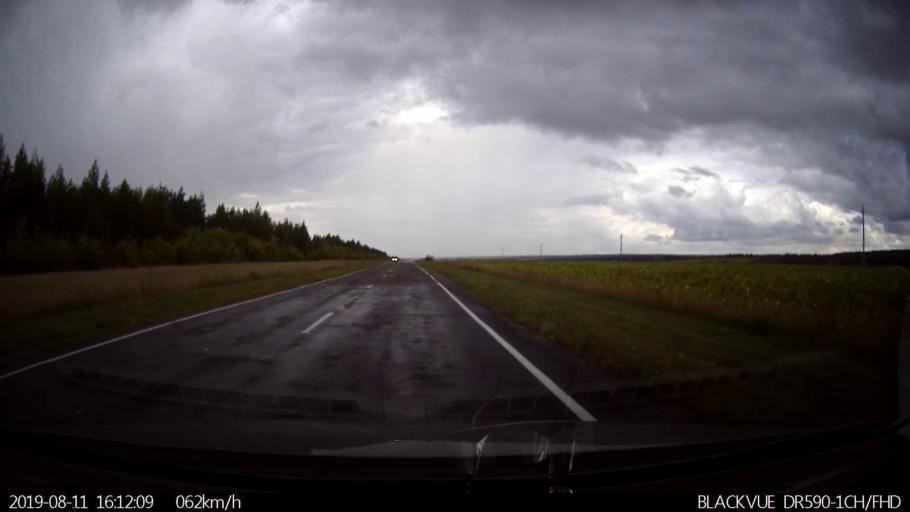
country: RU
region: Ulyanovsk
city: Ignatovka
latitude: 54.0090
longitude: 47.6414
